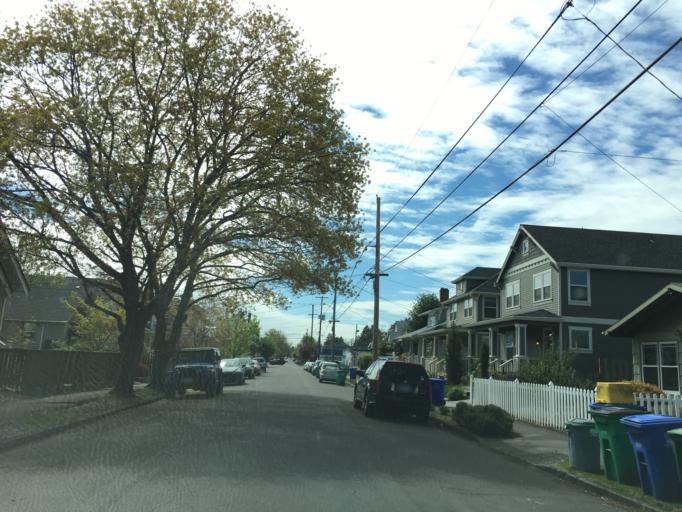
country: US
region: Oregon
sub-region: Multnomah County
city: Lents
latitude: 45.5279
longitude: -122.5824
